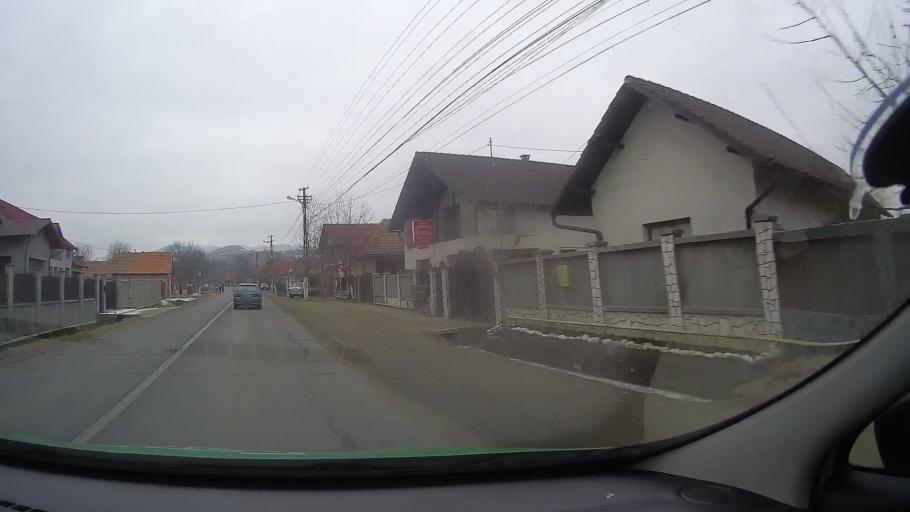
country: RO
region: Alba
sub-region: Comuna Ighiu
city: Sard
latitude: 46.1214
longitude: 23.5252
